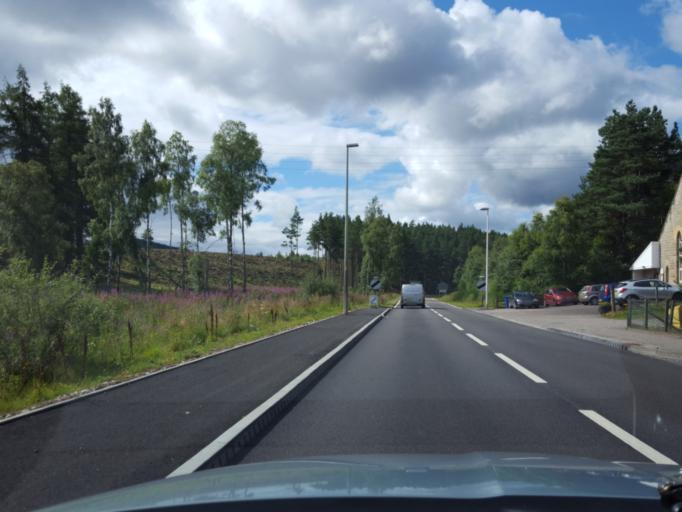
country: GB
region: Scotland
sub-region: Highland
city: Grantown on Spey
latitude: 57.3351
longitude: -3.5417
